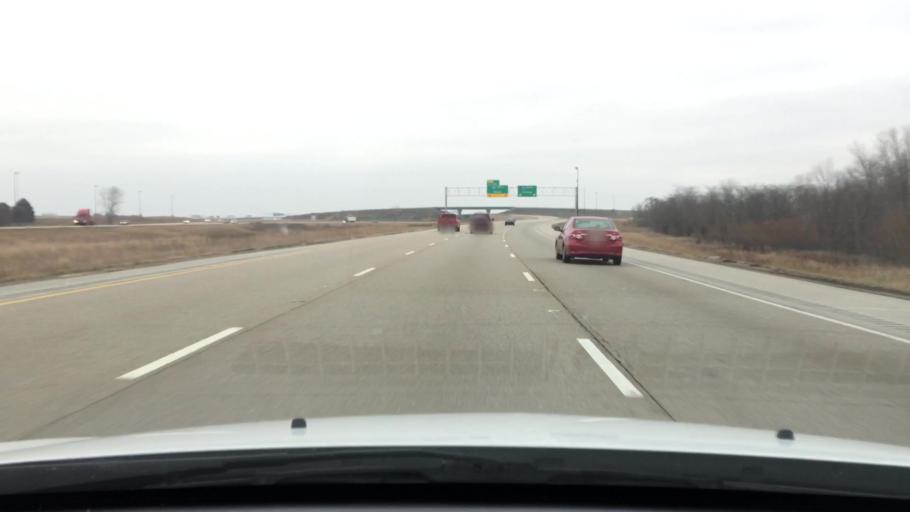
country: US
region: Illinois
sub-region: Logan County
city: Lincoln
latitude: 40.1705
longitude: -89.4174
